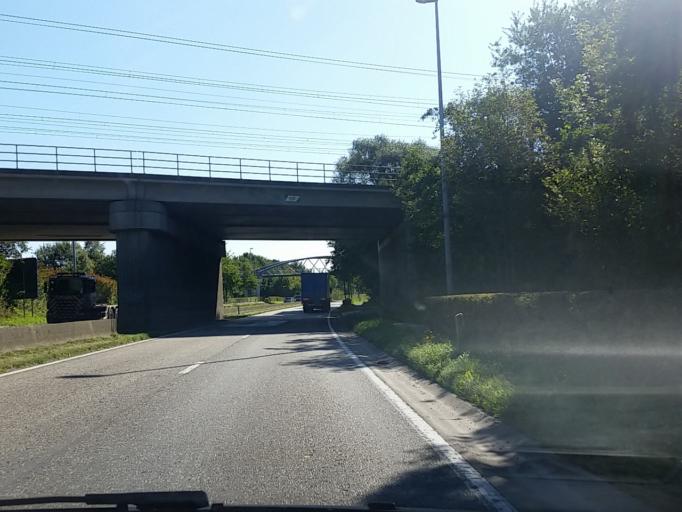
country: BE
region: Flanders
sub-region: Provincie Vlaams-Brabant
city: Vilvoorde
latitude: 50.9441
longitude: 4.4460
